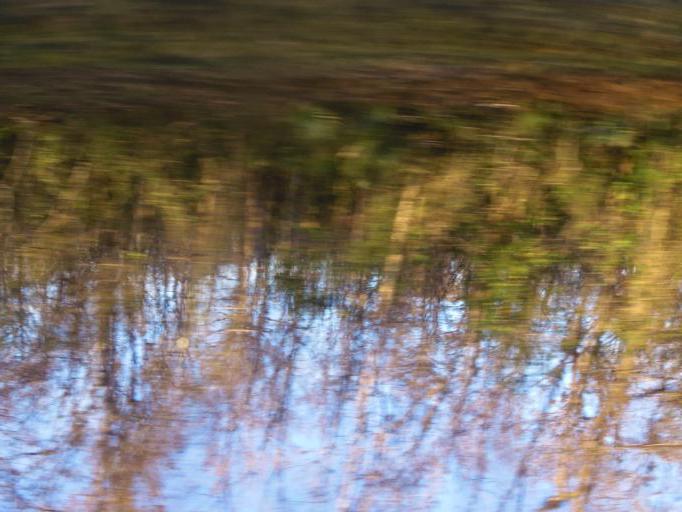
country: US
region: Florida
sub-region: Clay County
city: Green Cove Springs
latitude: 29.9606
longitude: -81.5424
